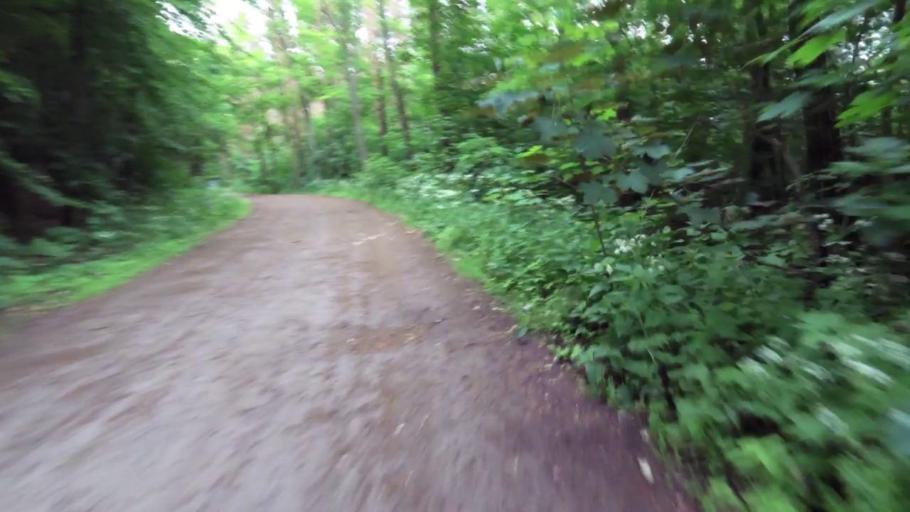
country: PL
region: West Pomeranian Voivodeship
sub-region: Powiat kamienski
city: Miedzyzdroje
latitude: 53.9268
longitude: 14.5367
